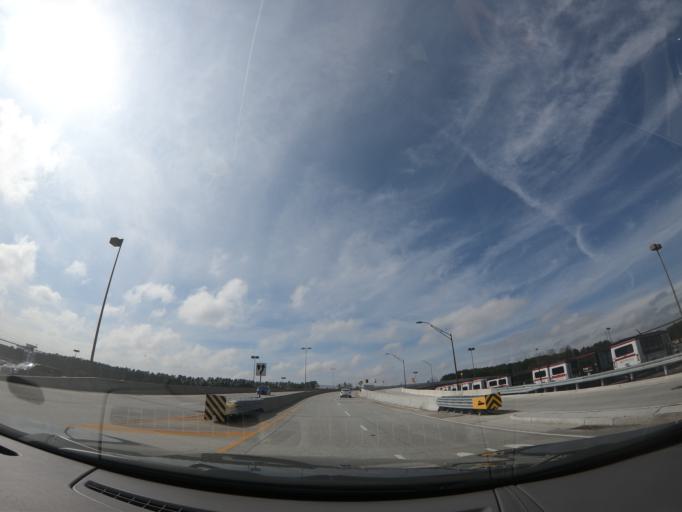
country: US
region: Georgia
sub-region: Fulton County
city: College Park
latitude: 33.6357
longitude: -84.4545
